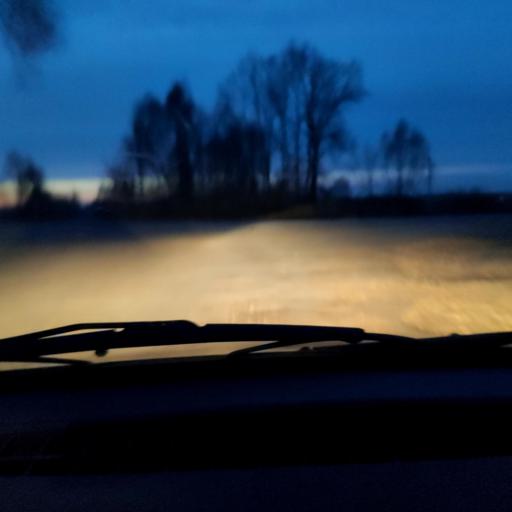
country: RU
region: Bashkortostan
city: Mikhaylovka
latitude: 54.7818
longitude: 55.8295
